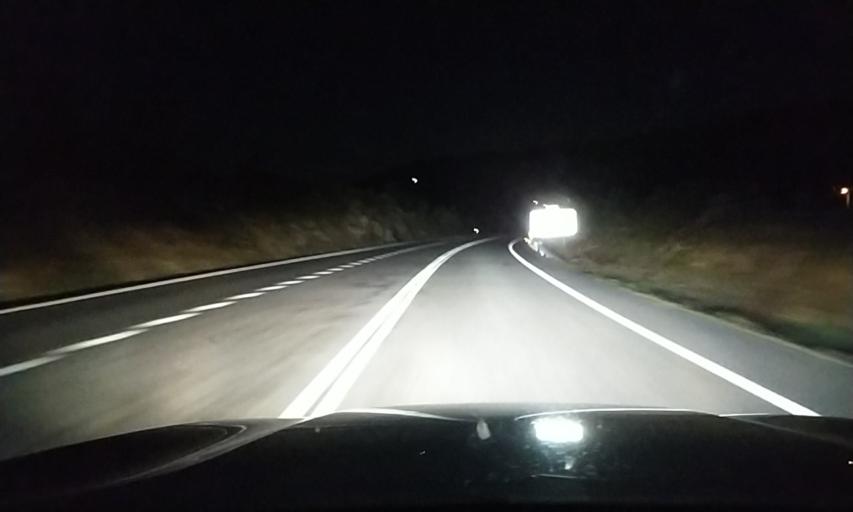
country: ES
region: Galicia
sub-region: Provincia de Ourense
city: Cualedro
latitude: 41.9741
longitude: -7.5199
